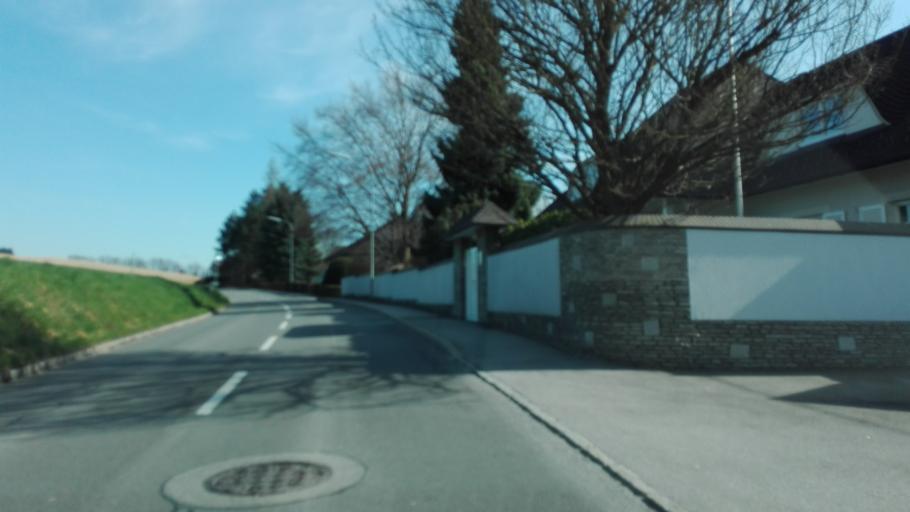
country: AT
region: Upper Austria
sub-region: Politischer Bezirk Perg
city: Perg
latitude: 48.2647
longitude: 14.5865
